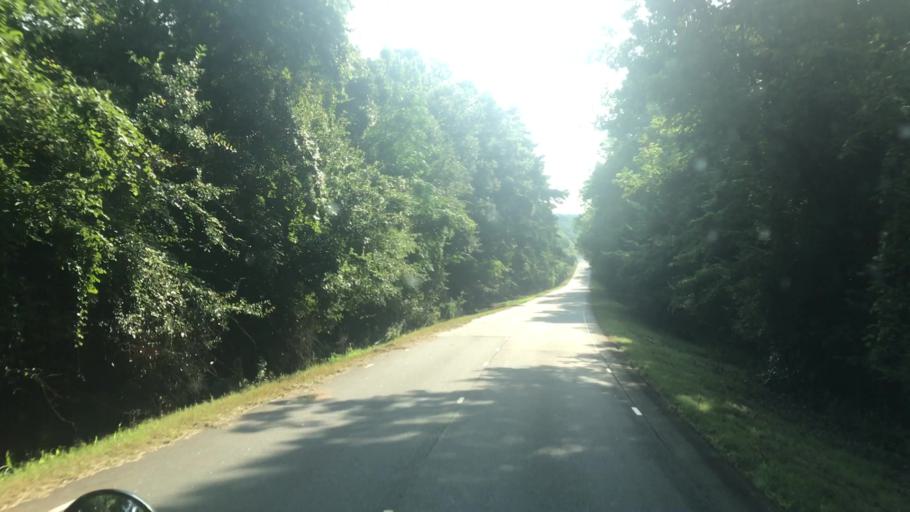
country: US
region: Florida
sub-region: Gadsden County
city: Havana
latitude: 30.7170
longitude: -84.4949
